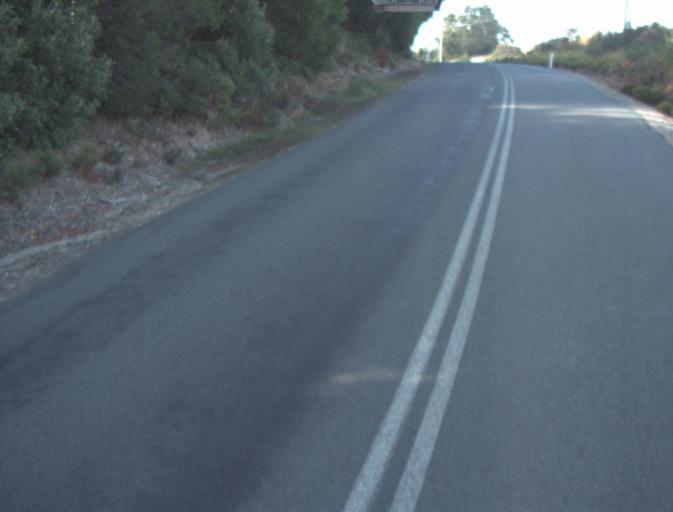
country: AU
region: Tasmania
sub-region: Launceston
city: Mayfield
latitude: -41.2055
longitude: 147.2150
